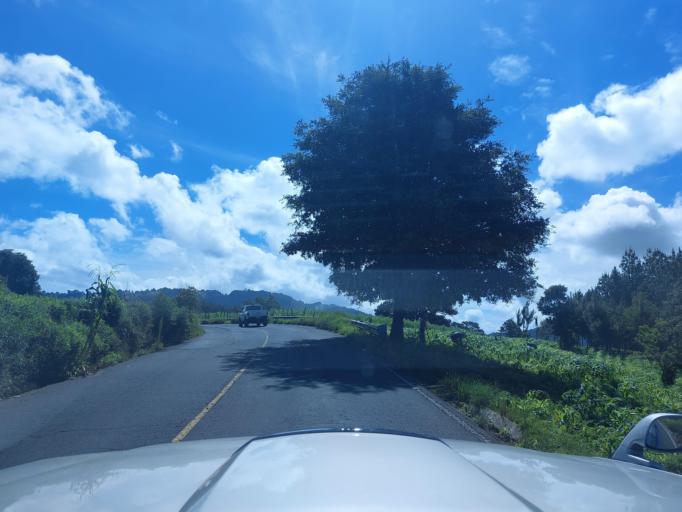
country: GT
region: Chimaltenango
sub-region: Municipio de Santa Cruz Balanya
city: Santa Cruz Balanya
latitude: 14.6995
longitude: -90.8997
